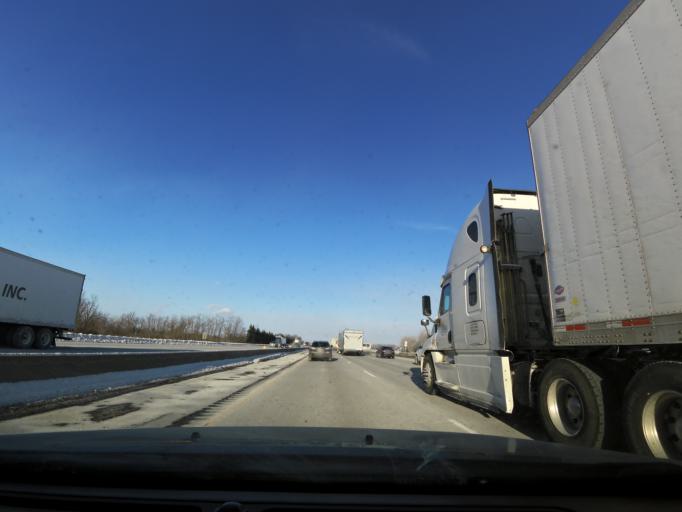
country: CA
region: Ontario
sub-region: Halton
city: Milton
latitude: 43.5746
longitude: -79.8255
